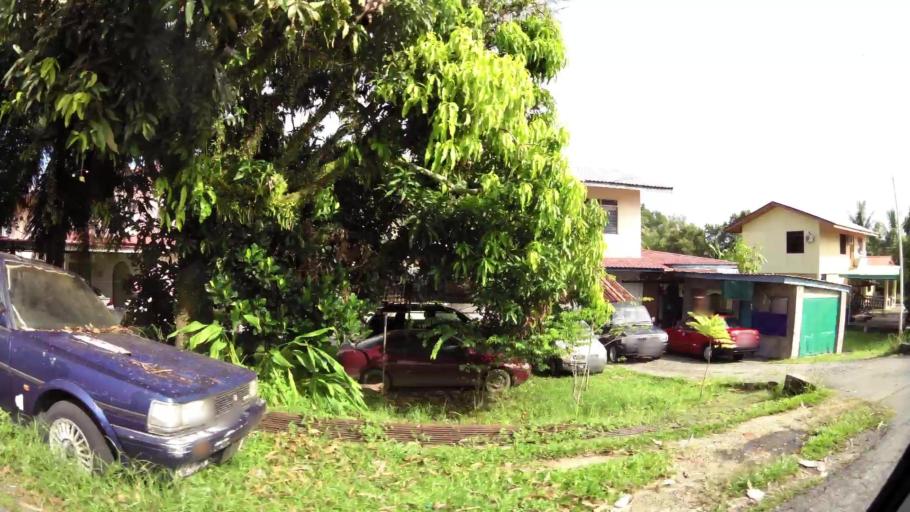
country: BN
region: Brunei and Muara
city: Bandar Seri Begawan
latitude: 4.9216
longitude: 114.8986
